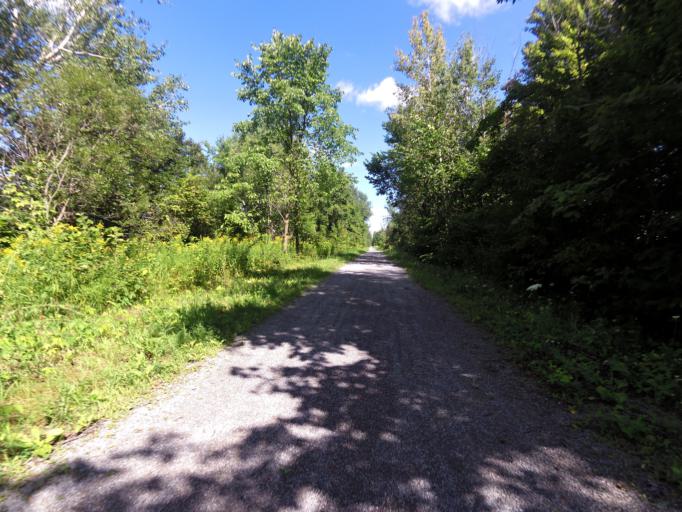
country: CA
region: Ontario
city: Ottawa
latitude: 45.1939
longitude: -75.6221
